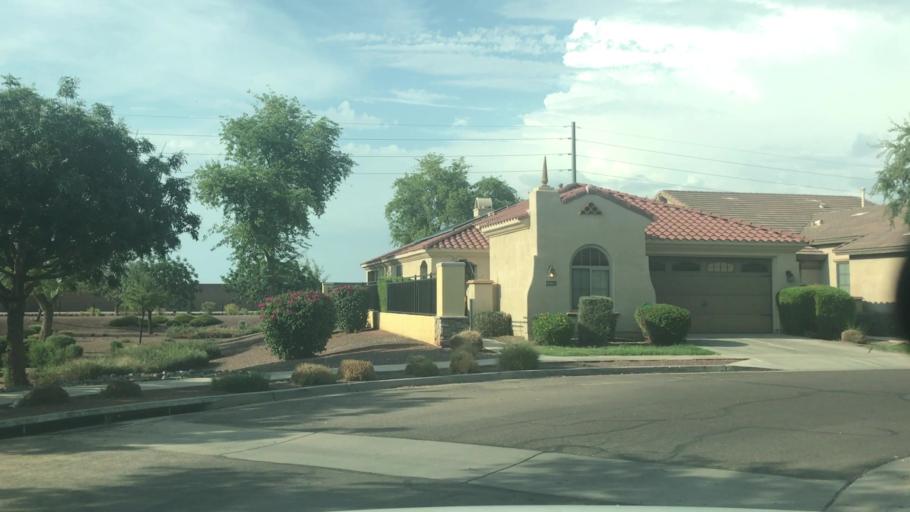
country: US
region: Arizona
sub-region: Maricopa County
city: Gilbert
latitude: 33.3264
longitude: -111.7197
